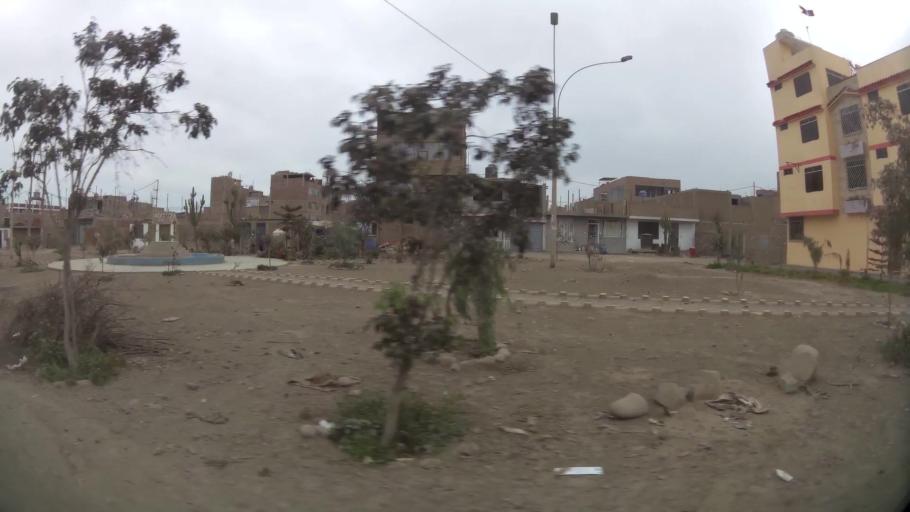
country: PE
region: Lima
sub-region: Lima
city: Independencia
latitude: -11.9577
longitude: -77.0963
